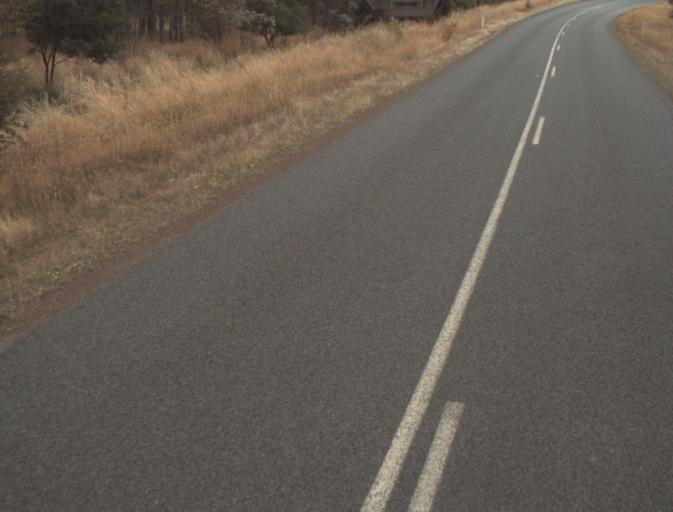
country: AU
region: Tasmania
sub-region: Northern Midlands
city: Evandale
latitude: -41.4841
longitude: 147.5036
